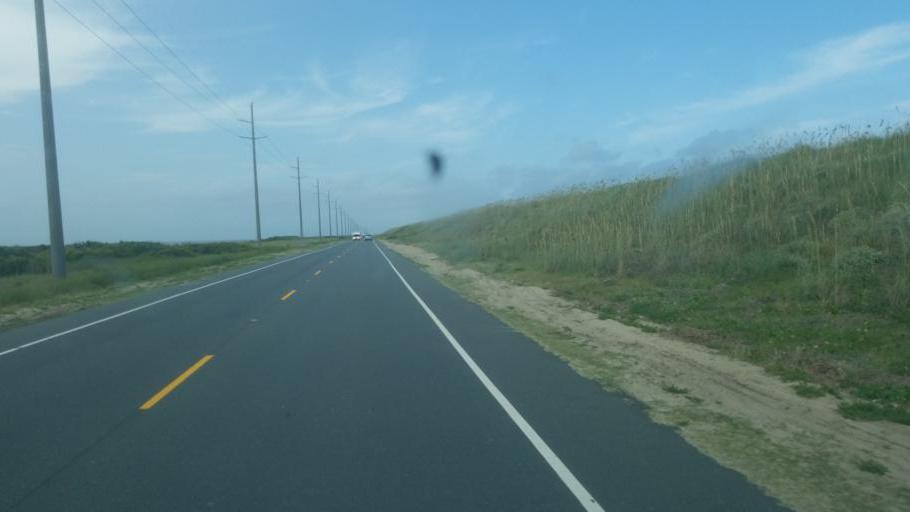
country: US
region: North Carolina
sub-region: Dare County
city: Buxton
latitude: 35.2750
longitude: -75.5180
